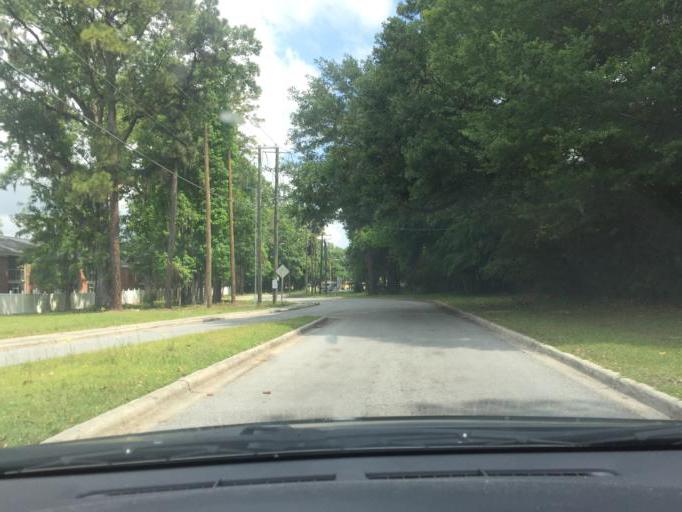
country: US
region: Georgia
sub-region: Chatham County
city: Montgomery
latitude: 31.9908
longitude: -81.1357
